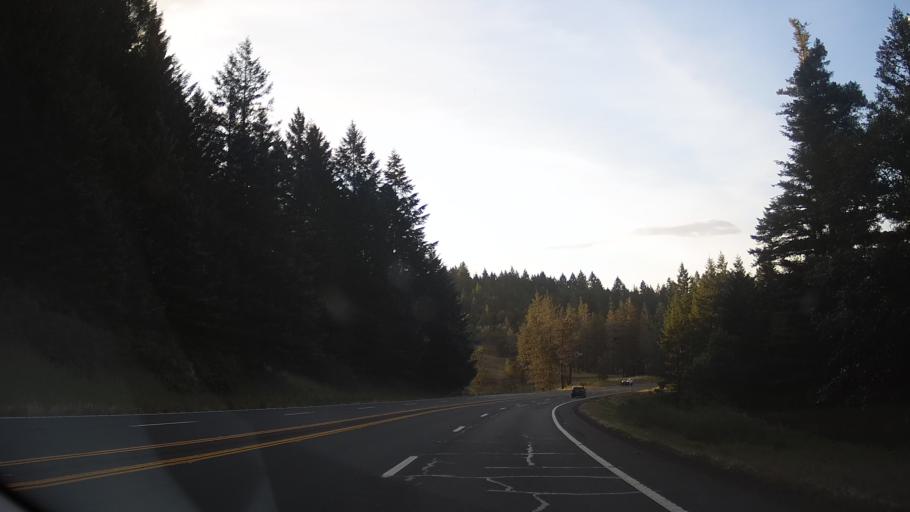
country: US
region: California
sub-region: Mendocino County
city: Willits
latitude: 39.3489
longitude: -123.3221
